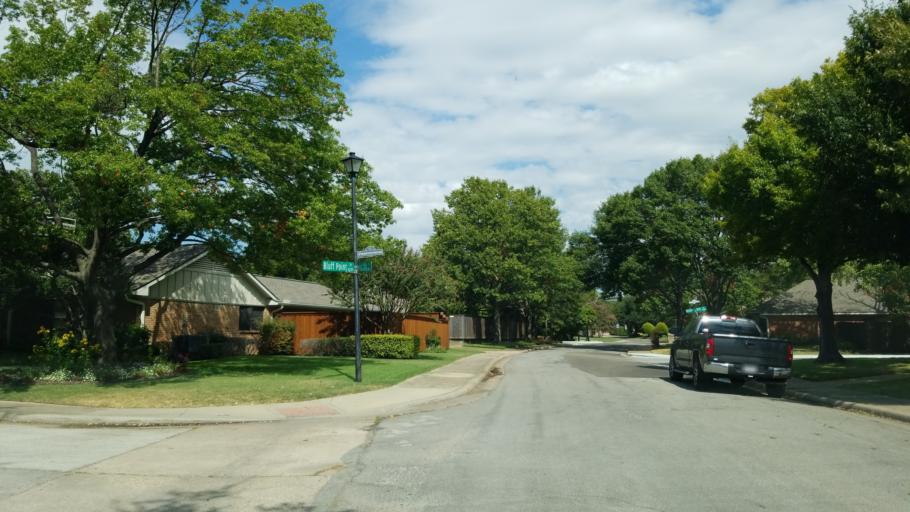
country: US
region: Texas
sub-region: Dallas County
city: Addison
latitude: 32.9612
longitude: -96.7981
